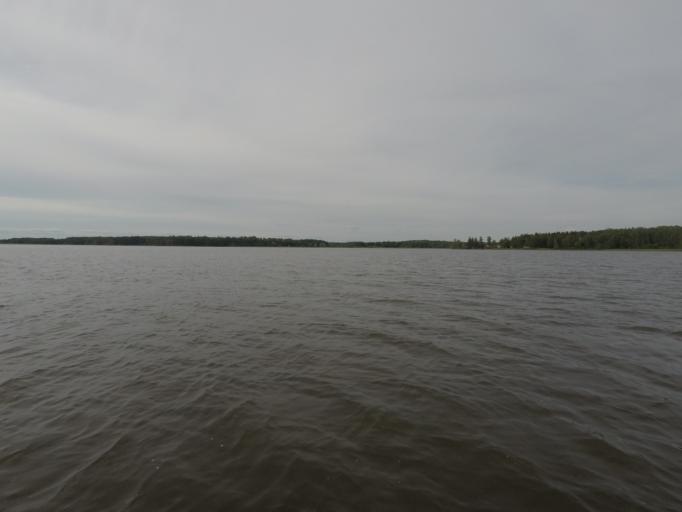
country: SE
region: Soedermanland
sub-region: Eskilstuna Kommun
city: Torshalla
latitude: 59.4832
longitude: 16.4156
